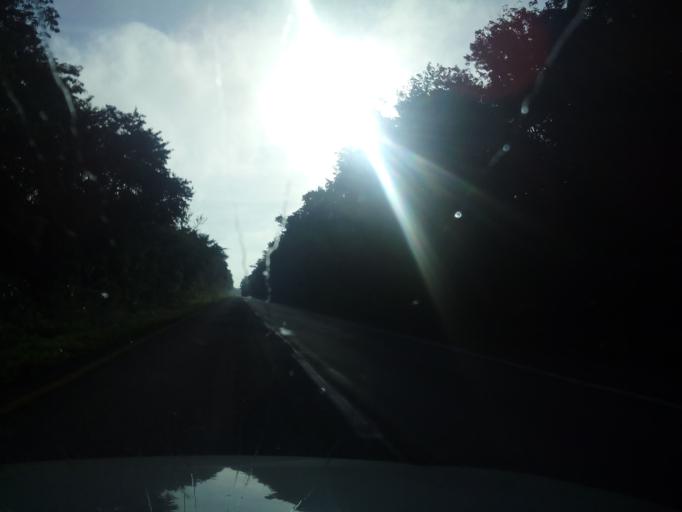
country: MX
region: Yucatan
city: Tunkas
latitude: 20.7664
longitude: -88.8088
